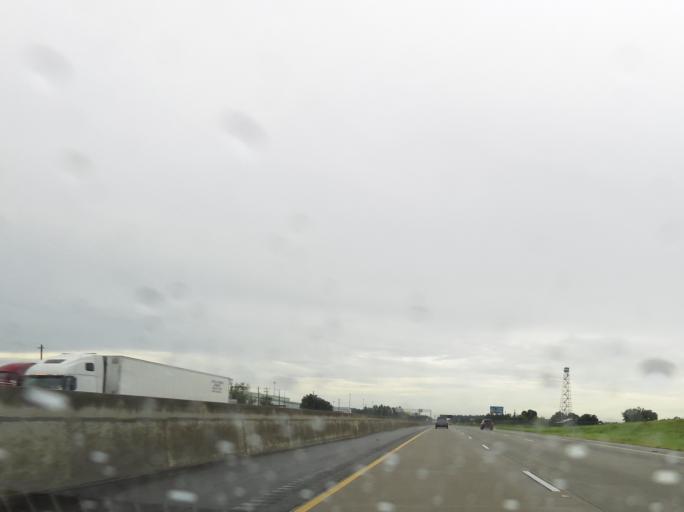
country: US
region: Georgia
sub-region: Cook County
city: Adel
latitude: 31.1121
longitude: -83.4276
